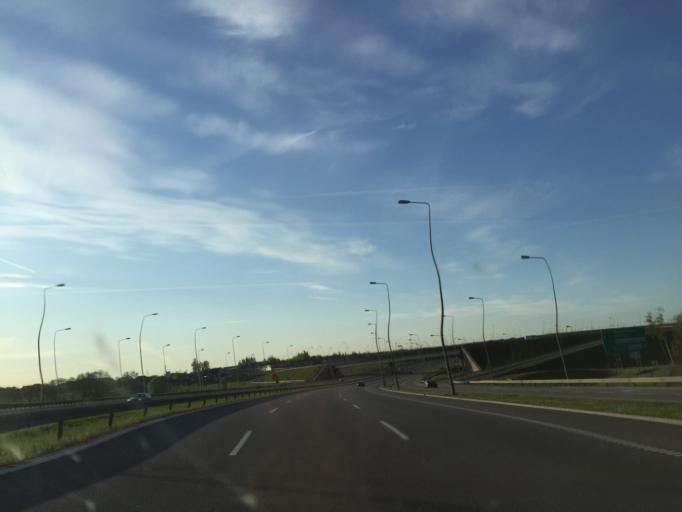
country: PL
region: Pomeranian Voivodeship
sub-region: Powiat gdanski
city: Kowale
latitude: 54.3443
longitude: 18.5208
